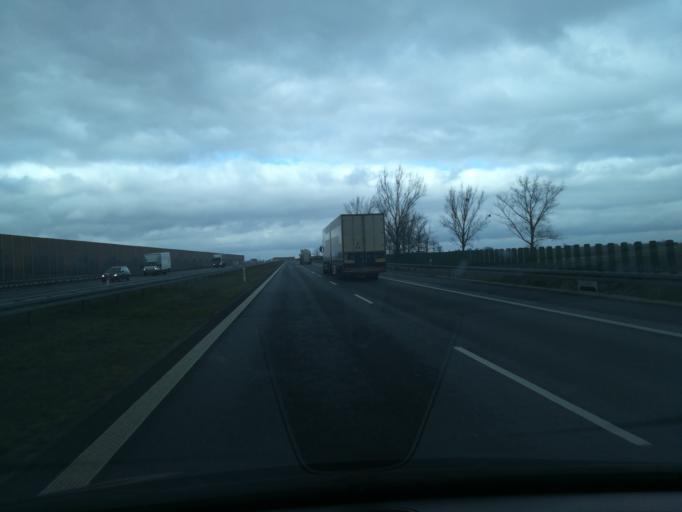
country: PL
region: Kujawsko-Pomorskie
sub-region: Powiat aleksandrowski
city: Raciazek
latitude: 52.8126
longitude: 18.8118
